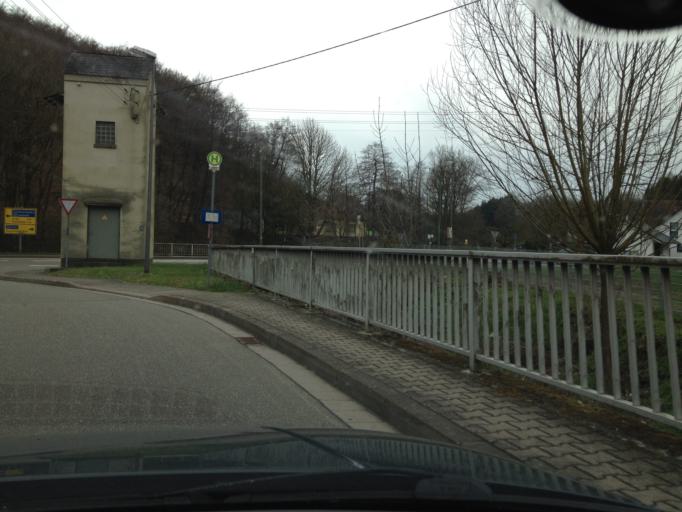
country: DE
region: Rheinland-Pfalz
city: Thallichtenberg
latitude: 49.5549
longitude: 7.3501
